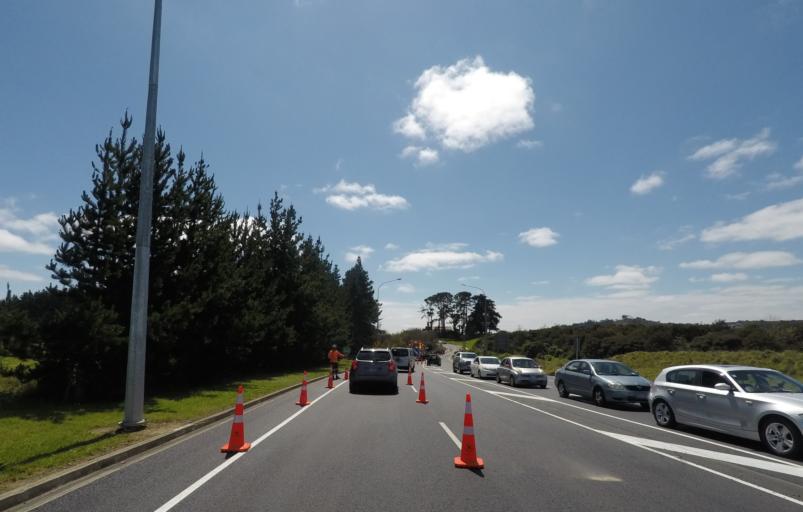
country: NZ
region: Auckland
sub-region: Auckland
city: Manukau City
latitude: -36.9642
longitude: 174.9067
